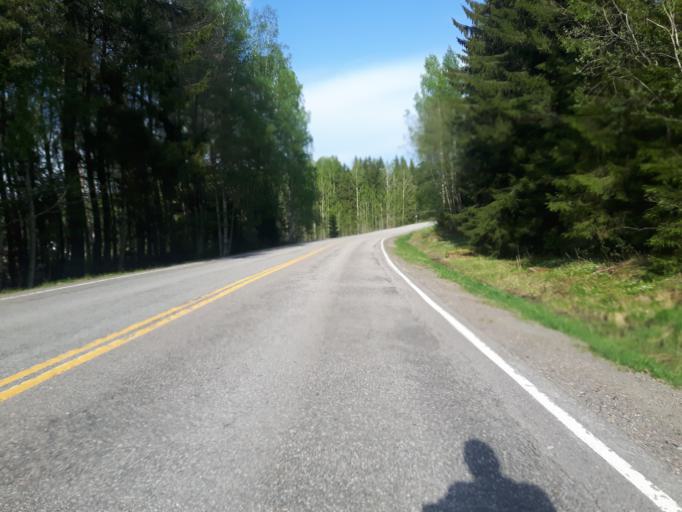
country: FI
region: Uusimaa
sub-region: Porvoo
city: Porvoo
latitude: 60.4820
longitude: 25.8213
